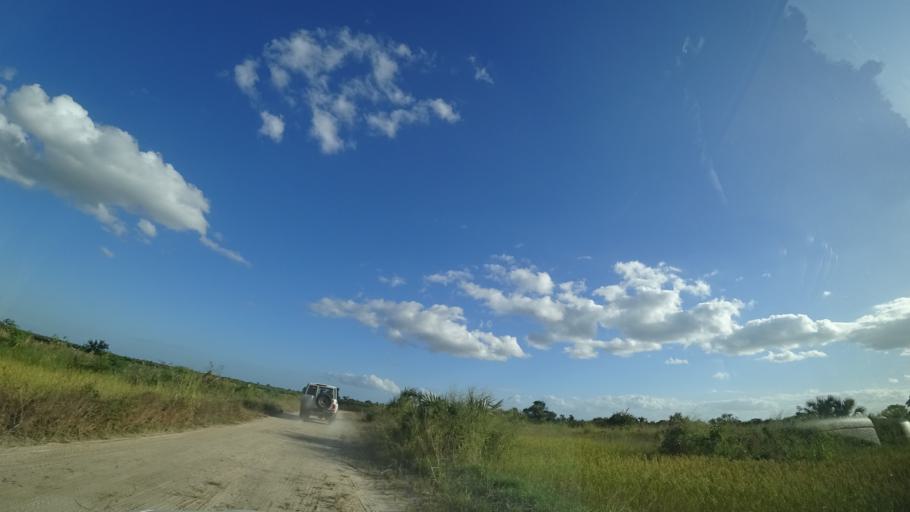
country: MZ
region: Sofala
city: Dondo
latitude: -19.4191
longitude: 34.5649
